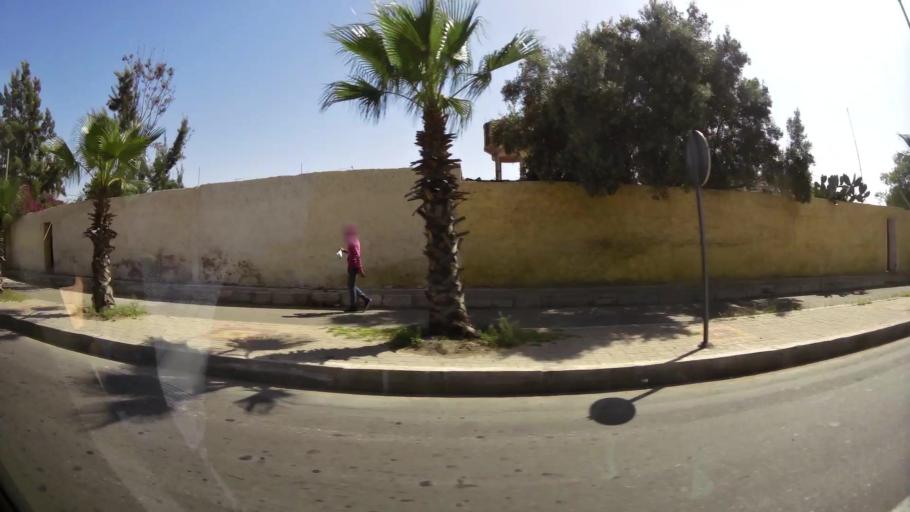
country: MA
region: Souss-Massa-Draa
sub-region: Inezgane-Ait Mellou
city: Inezgane
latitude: 30.3657
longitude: -9.5440
